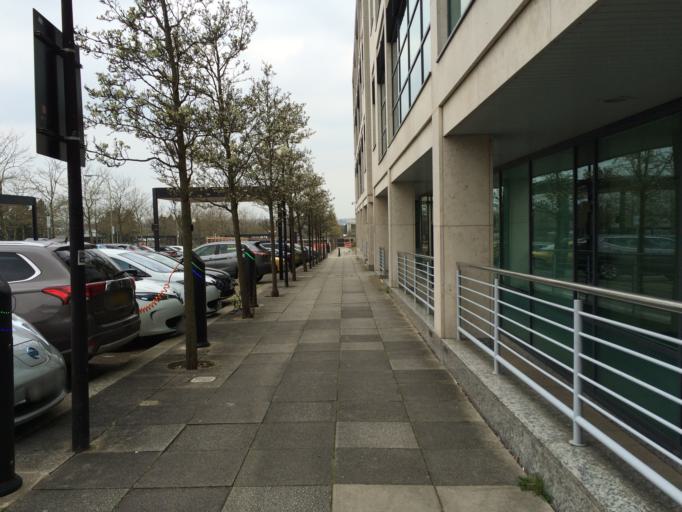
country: GB
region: England
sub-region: Milton Keynes
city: Milton Keynes
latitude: 52.0362
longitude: -0.7649
